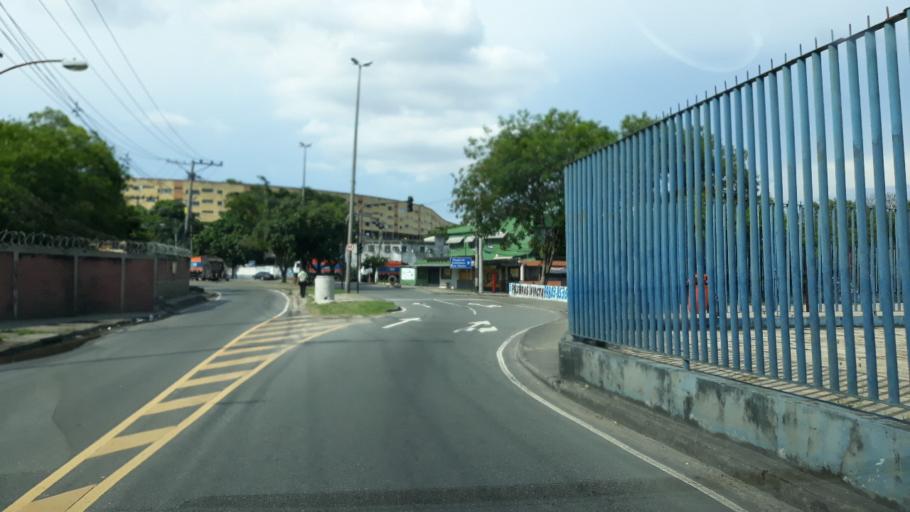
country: BR
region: Rio de Janeiro
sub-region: Sao Joao De Meriti
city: Sao Joao de Meriti
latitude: -22.8522
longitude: -43.3841
